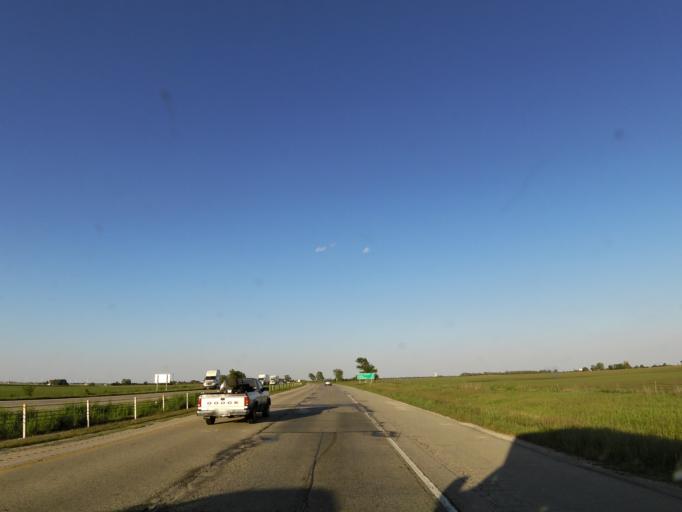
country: US
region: Illinois
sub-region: Champaign County
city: Homer
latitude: 40.1200
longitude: -87.9382
